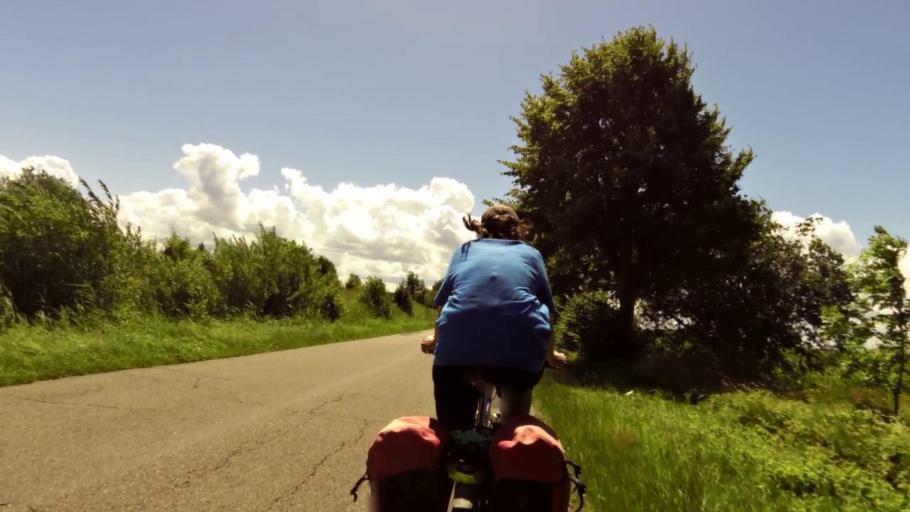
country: PL
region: West Pomeranian Voivodeship
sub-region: Powiat koszalinski
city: Sianow
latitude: 54.2921
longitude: 16.2105
